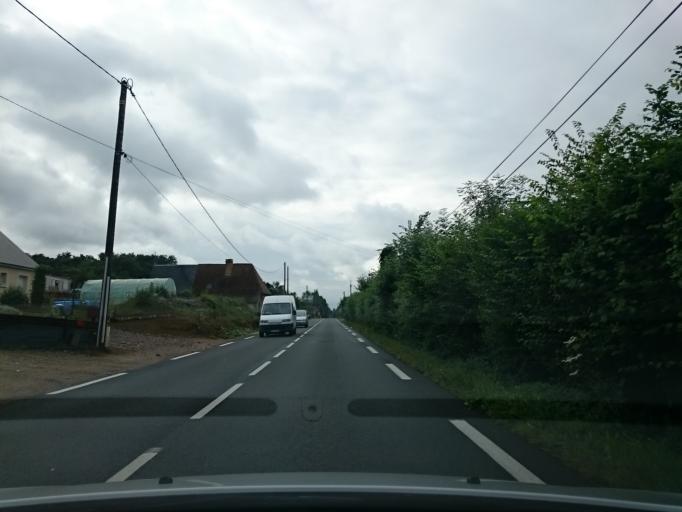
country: FR
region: Lower Normandy
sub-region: Departement du Calvados
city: Beuvillers
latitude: 49.1029
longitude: 0.2957
